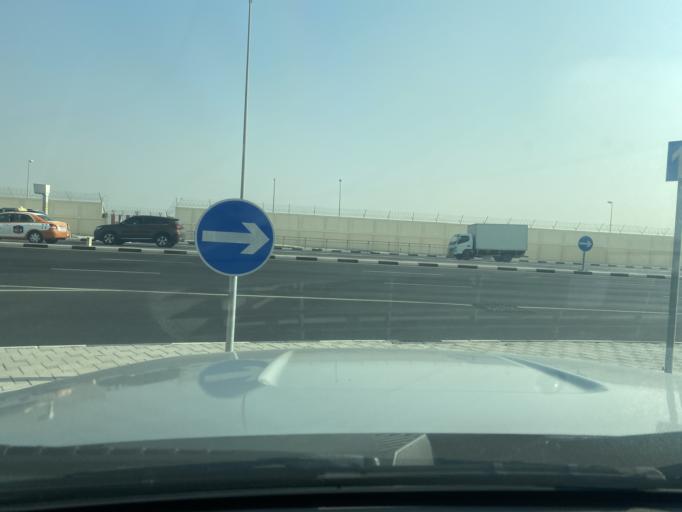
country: QA
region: Baladiyat ad Dawhah
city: Doha
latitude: 25.2450
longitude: 51.5683
